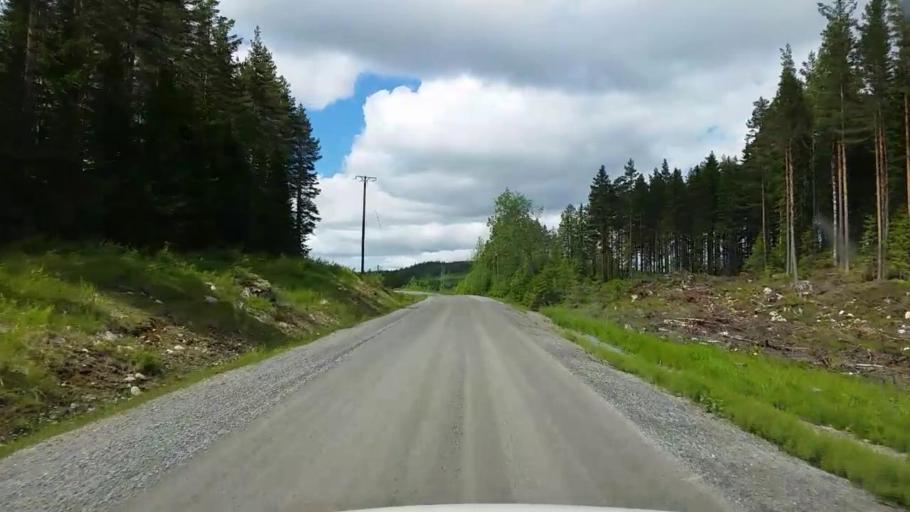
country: SE
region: Gaevleborg
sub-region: Bollnas Kommun
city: Vittsjo
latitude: 61.0892
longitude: 16.2479
